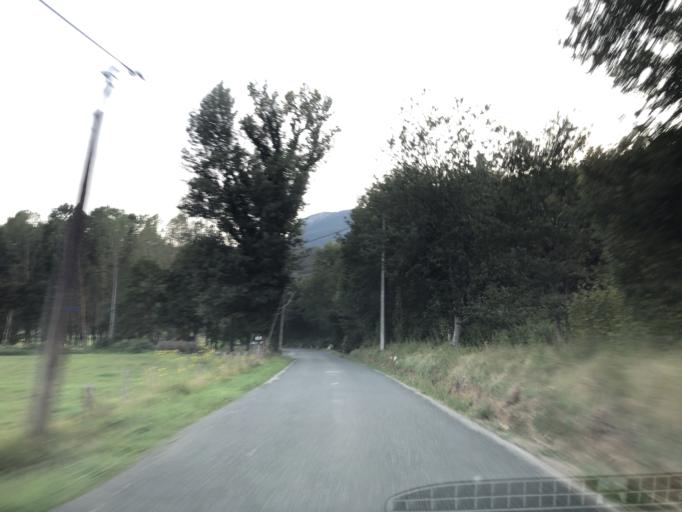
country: FR
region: Rhone-Alpes
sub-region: Departement de l'Ain
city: Virieu-le-Grand
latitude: 45.7954
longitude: 5.6262
